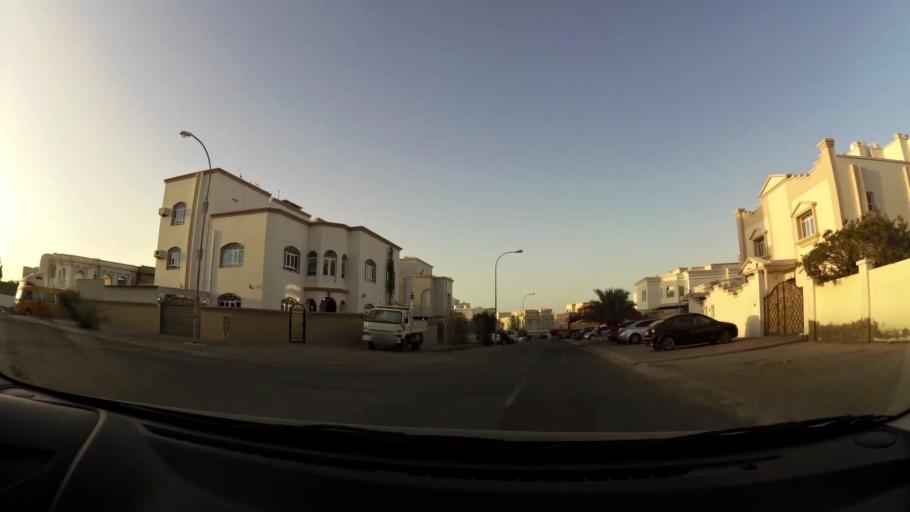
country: OM
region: Muhafazat Masqat
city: As Sib al Jadidah
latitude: 23.6052
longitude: 58.2295
